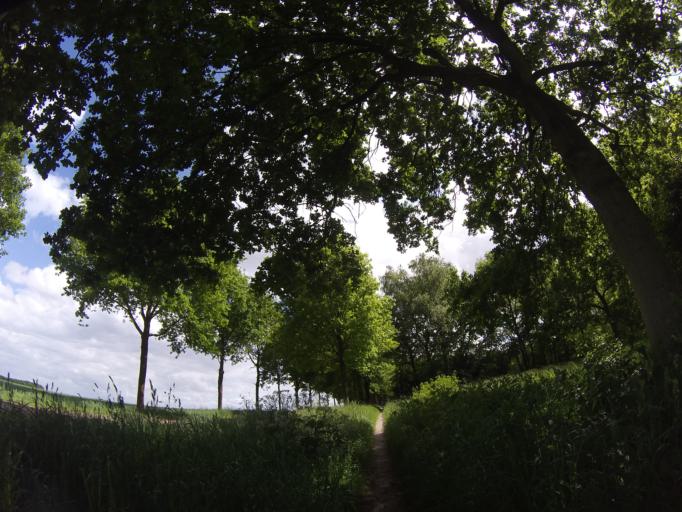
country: NL
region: Drenthe
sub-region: Gemeente Borger-Odoorn
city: Borger
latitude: 52.8804
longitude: 6.8701
